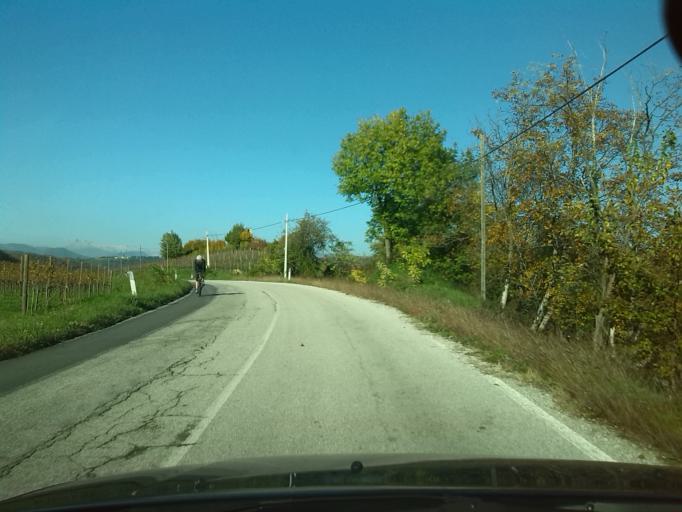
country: IT
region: Friuli Venezia Giulia
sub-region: Provincia di Gorizia
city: Dolegna del Collio
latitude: 46.0365
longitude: 13.4778
